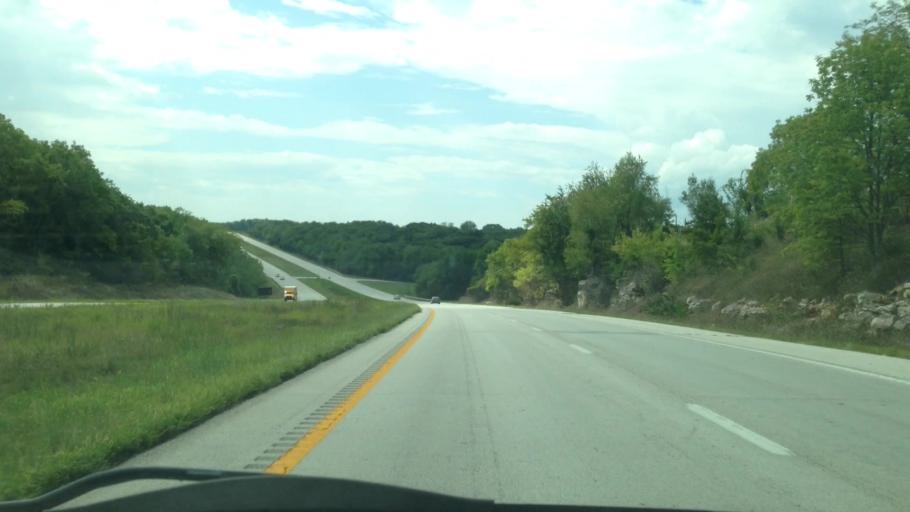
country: US
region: Missouri
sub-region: Marion County
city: Hannibal
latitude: 39.7431
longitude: -91.4244
